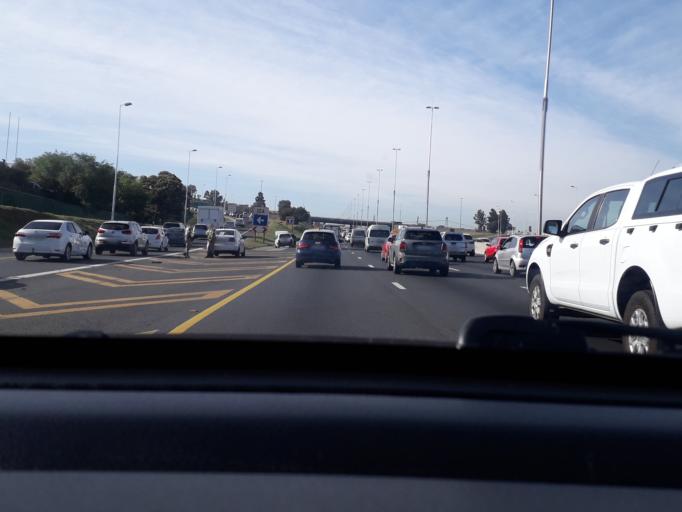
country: ZA
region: Gauteng
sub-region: City of Johannesburg Metropolitan Municipality
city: Modderfontein
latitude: -26.0775
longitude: 28.1134
